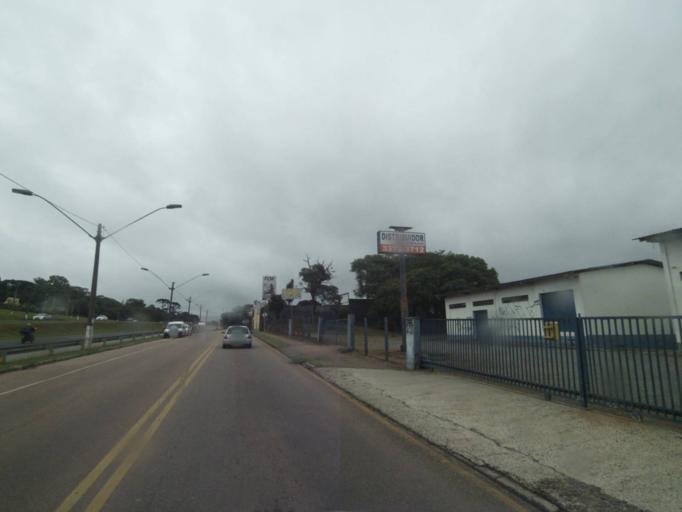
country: BR
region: Parana
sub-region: Curitiba
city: Curitiba
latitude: -25.4303
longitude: -49.3378
